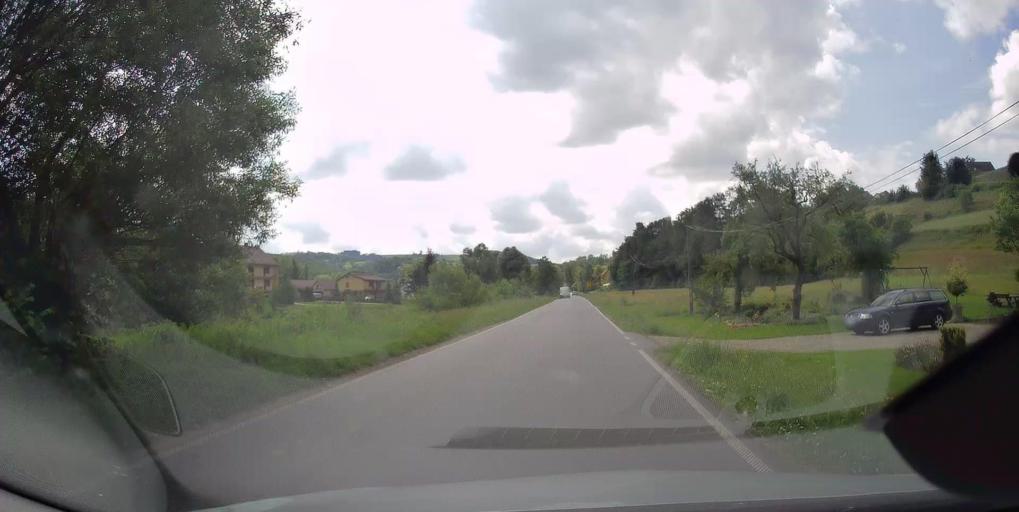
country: PL
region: Lesser Poland Voivodeship
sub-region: Powiat nowosadecki
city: Korzenna
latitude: 49.7403
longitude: 20.7700
